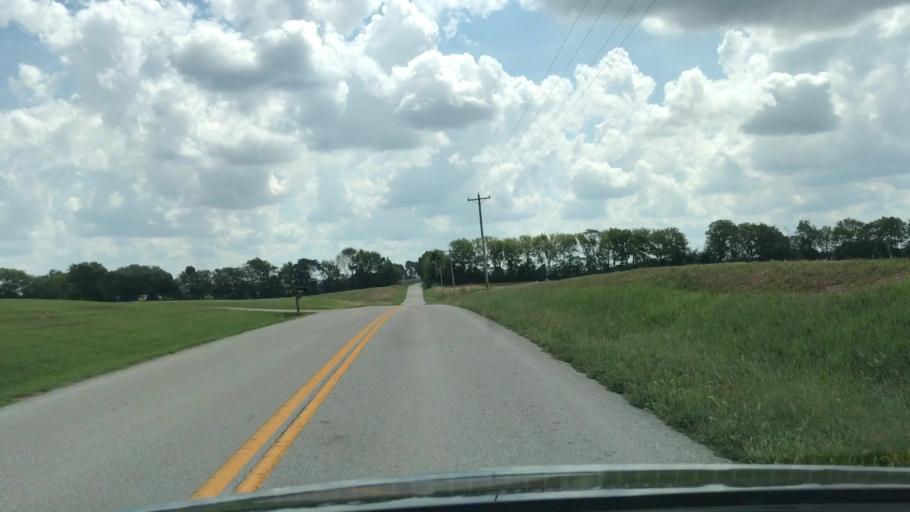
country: US
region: Kentucky
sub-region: Todd County
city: Elkton
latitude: 36.7849
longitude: -87.1284
